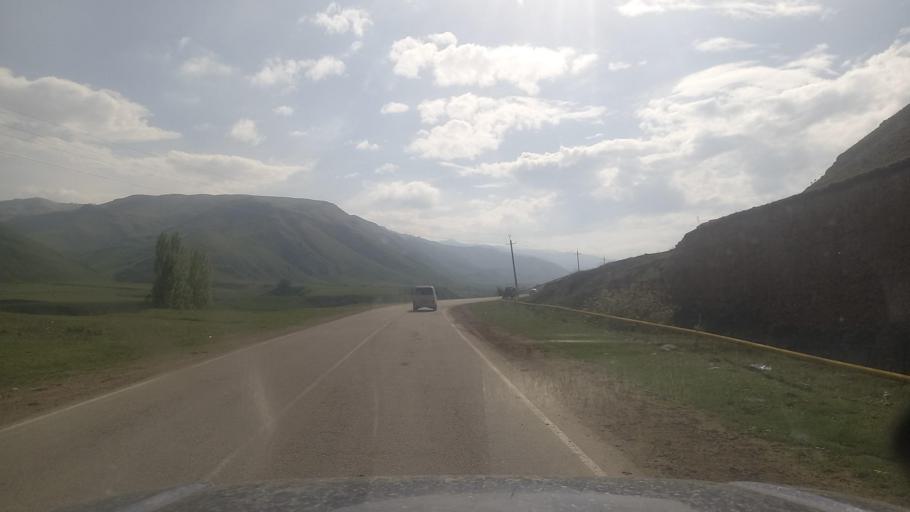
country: RU
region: Kabardino-Balkariya
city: Kamennomostskoye
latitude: 43.7346
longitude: 42.9712
